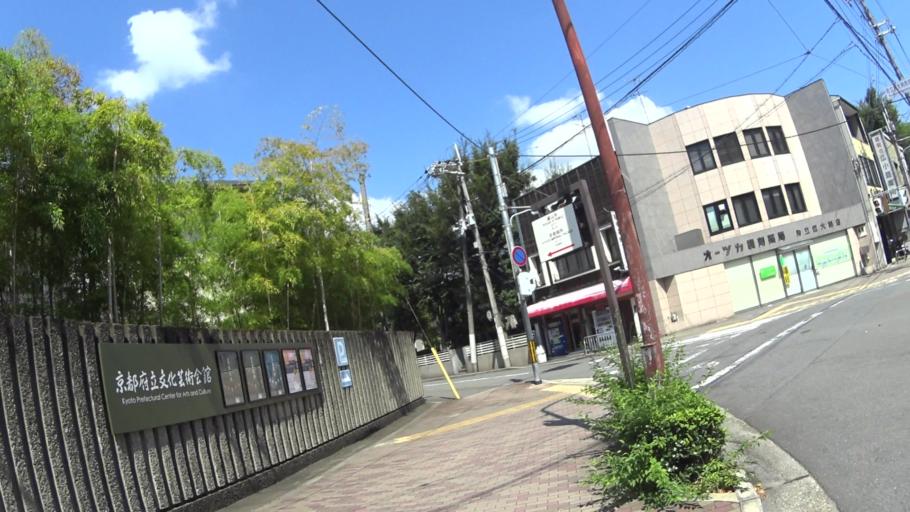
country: JP
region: Kyoto
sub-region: Kyoto-shi
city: Kamigyo-ku
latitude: 35.0231
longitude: 135.7692
